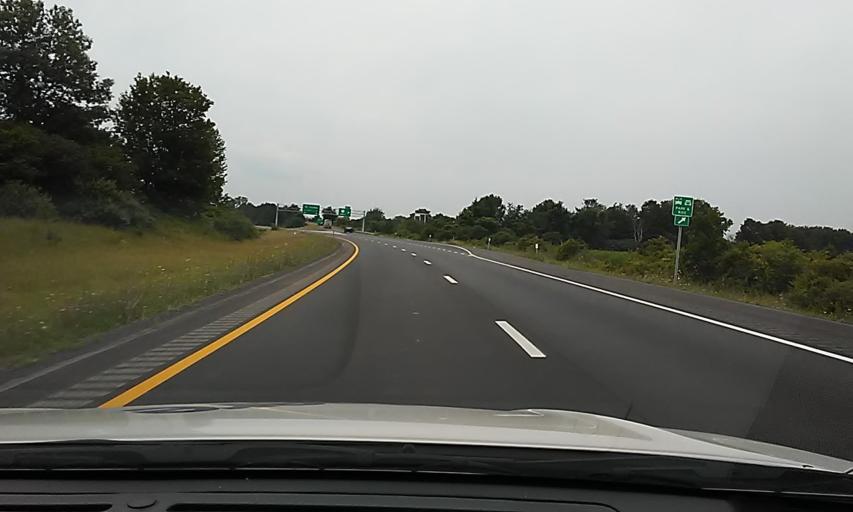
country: US
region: New York
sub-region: Genesee County
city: Bergen
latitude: 43.0384
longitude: -77.9613
